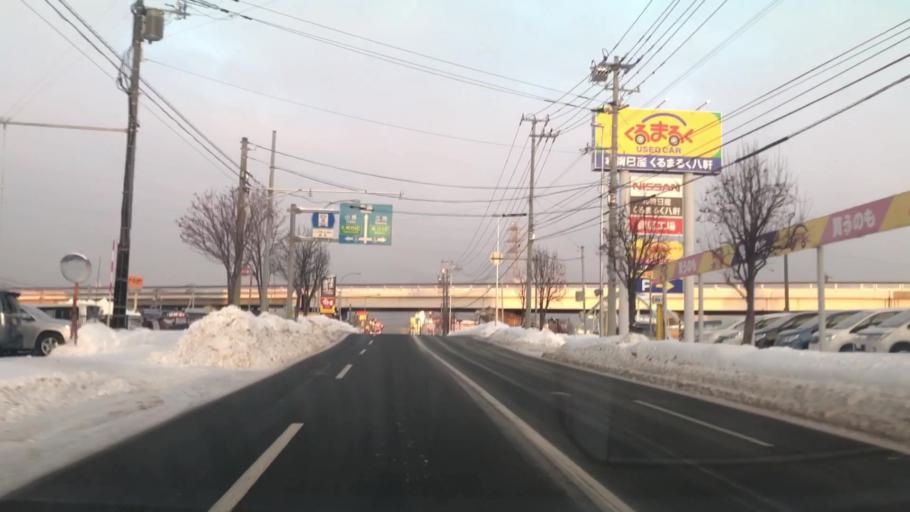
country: JP
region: Hokkaido
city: Sapporo
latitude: 43.0962
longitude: 141.2995
